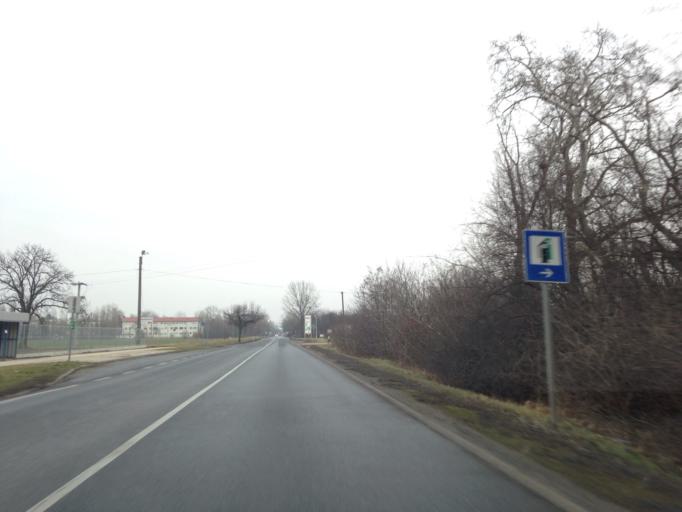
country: HU
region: Komarom-Esztergom
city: Almasfuzito
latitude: 47.7330
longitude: 18.2085
